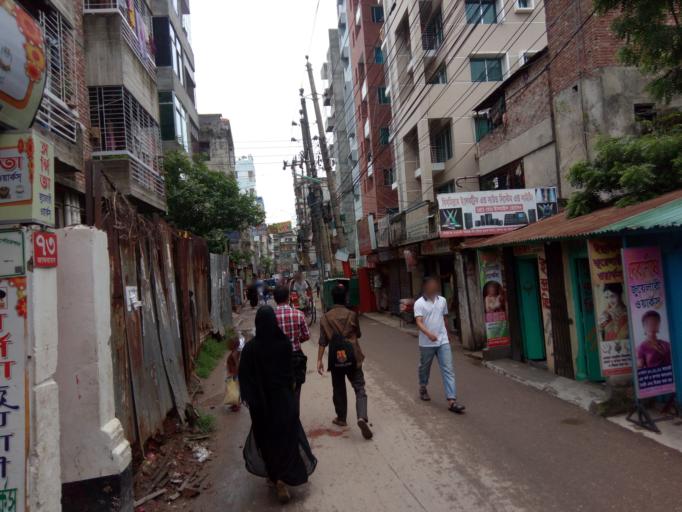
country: BD
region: Dhaka
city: Azimpur
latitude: 23.7501
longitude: 90.3633
